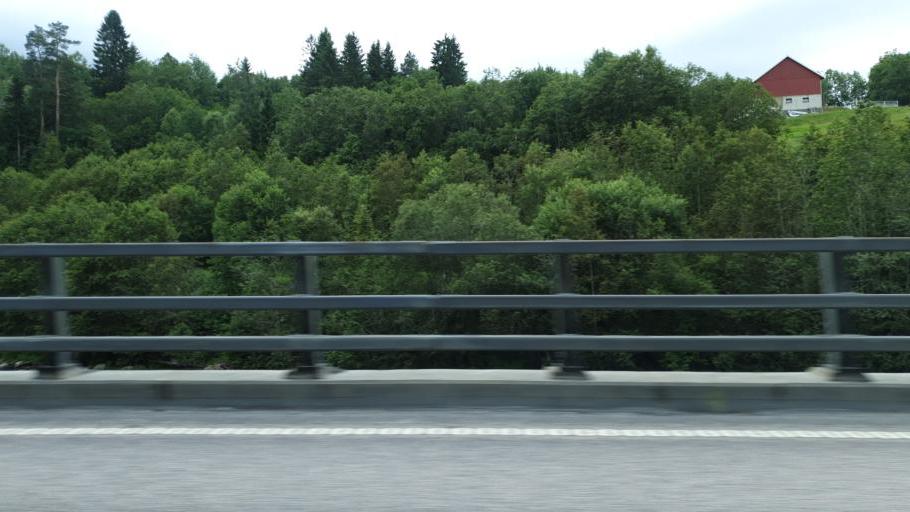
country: NO
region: Sor-Trondelag
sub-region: Midtre Gauldal
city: Storen
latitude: 62.9834
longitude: 10.2383
